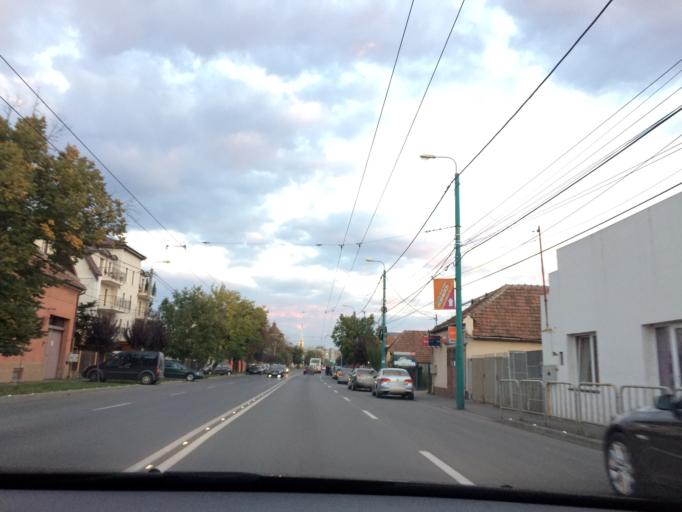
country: RO
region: Timis
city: Timisoara
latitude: 45.7661
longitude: 21.1993
